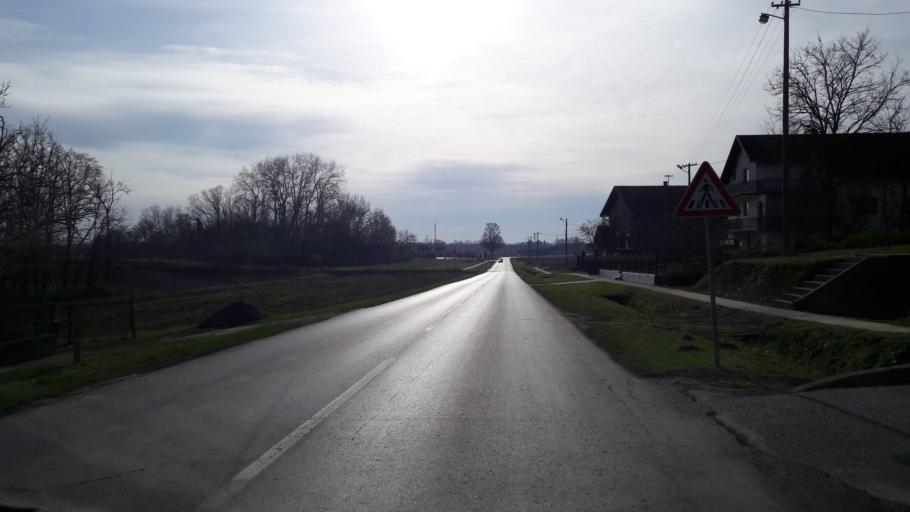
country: HR
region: Vukovarsko-Srijemska
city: Vodinci
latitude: 45.3007
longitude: 18.5605
